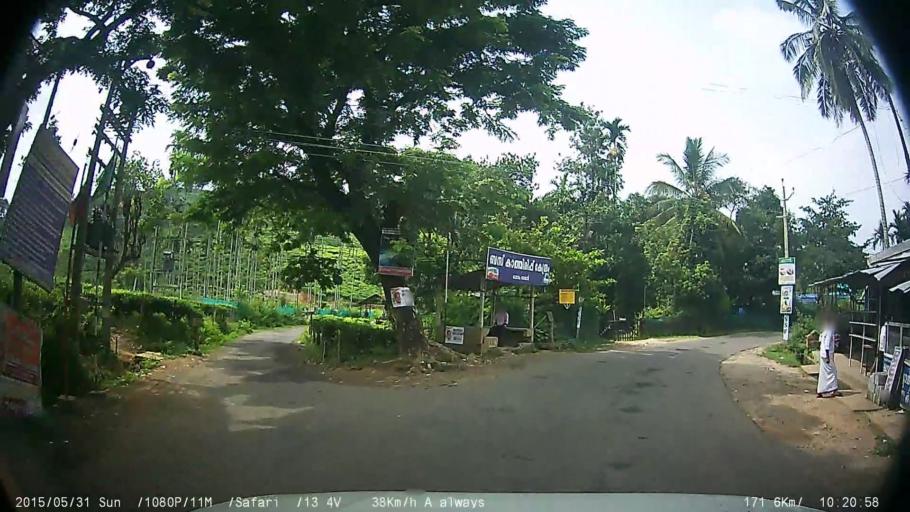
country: IN
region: Kerala
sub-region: Wayanad
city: Kalpetta
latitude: 11.5430
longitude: 76.1386
